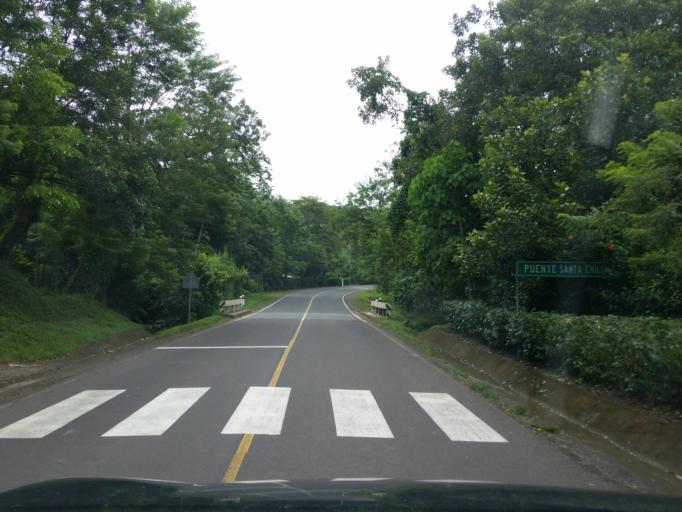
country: NI
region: Matagalpa
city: San Ramon
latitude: 12.9821
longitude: -85.8391
